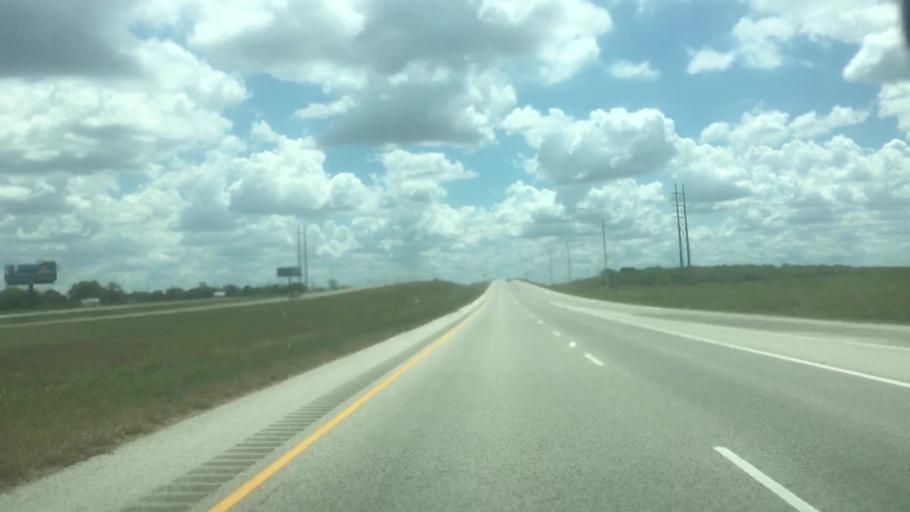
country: US
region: Texas
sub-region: Caldwell County
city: Uhland
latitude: 30.0113
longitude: -97.6881
